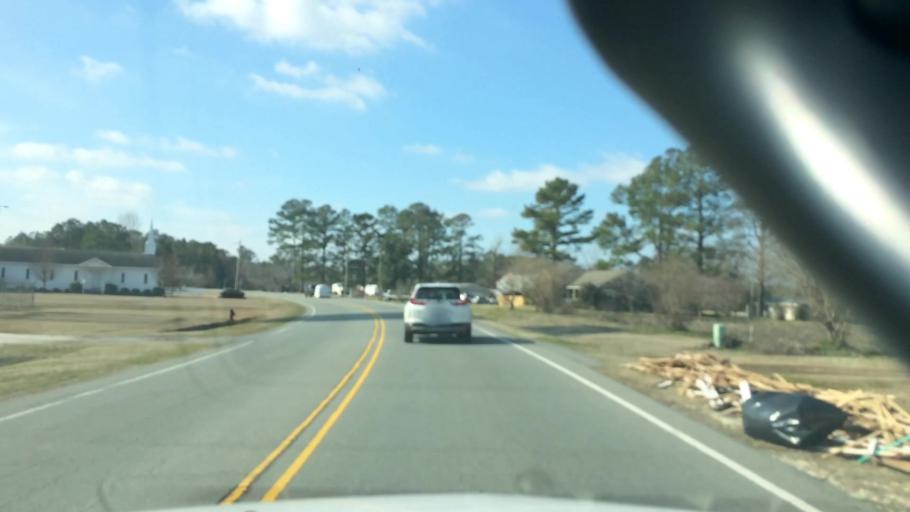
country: US
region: North Carolina
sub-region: Duplin County
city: Beulaville
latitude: 34.8338
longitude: -77.8243
